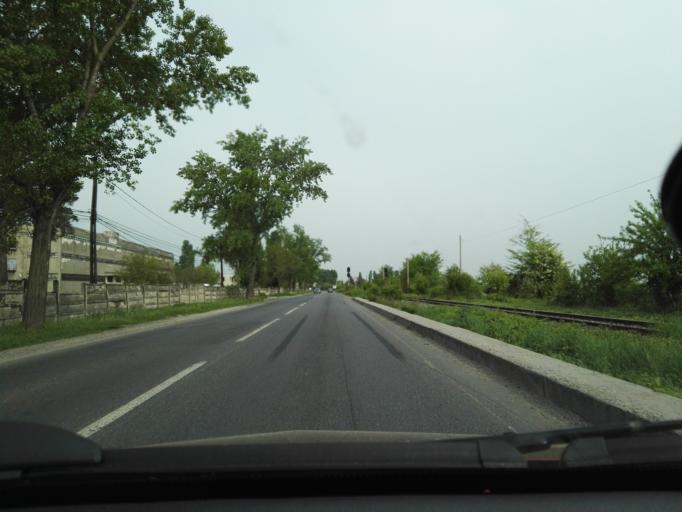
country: RO
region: Ilfov
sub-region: Comuna Magurele
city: Magurele
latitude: 44.3643
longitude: 26.0224
